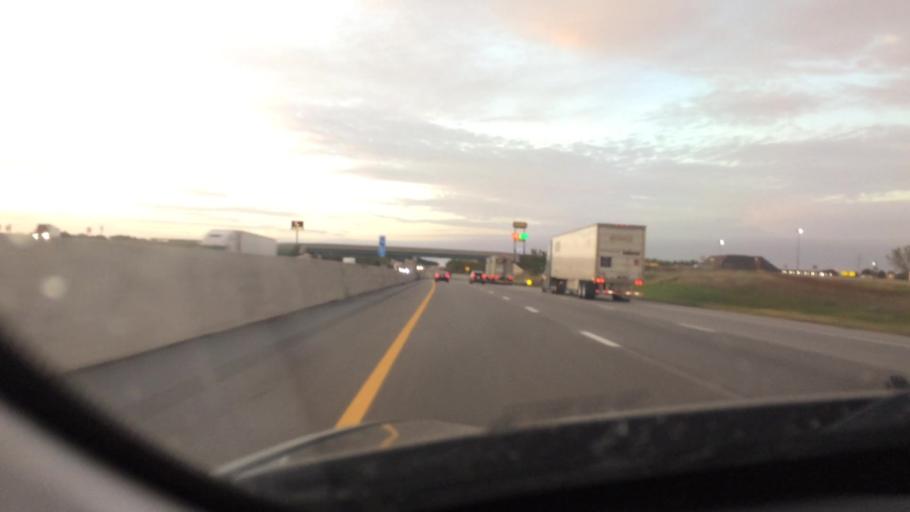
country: US
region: Ohio
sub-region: Wood County
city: North Baltimore
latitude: 41.1398
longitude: -83.6590
